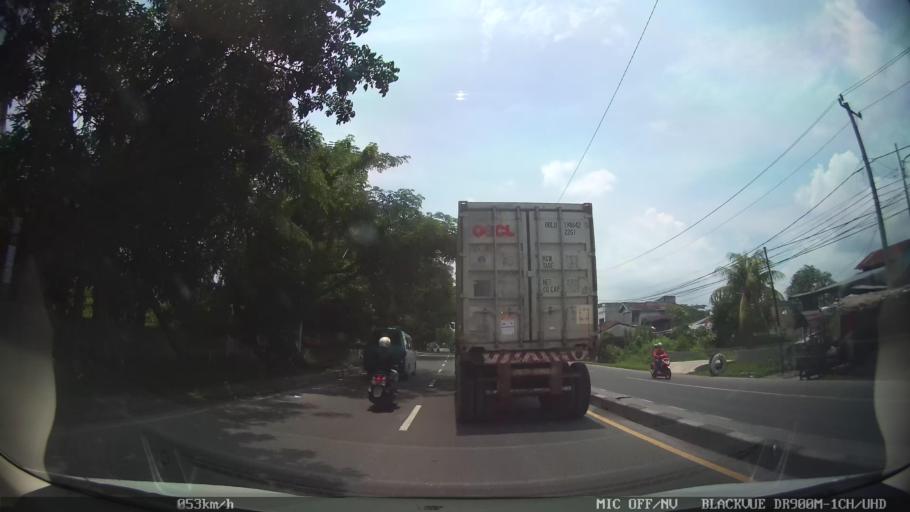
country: ID
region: North Sumatra
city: Labuhan Deli
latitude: 3.7293
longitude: 98.6766
